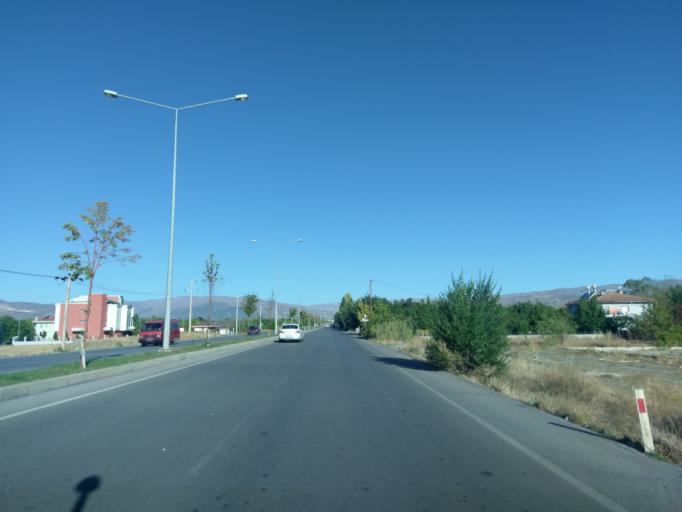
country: TR
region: Erzincan
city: Erzincan
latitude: 39.7680
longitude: 39.4300
